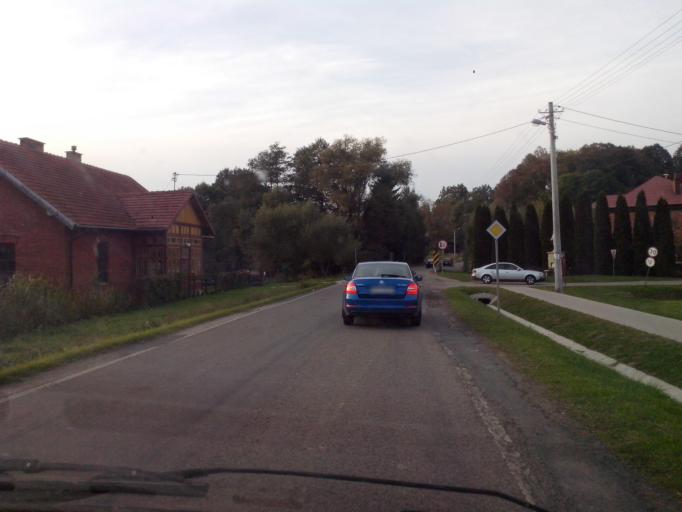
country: PL
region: Subcarpathian Voivodeship
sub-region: Powiat strzyzowski
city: Jawornik
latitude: 49.8152
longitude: 21.8414
